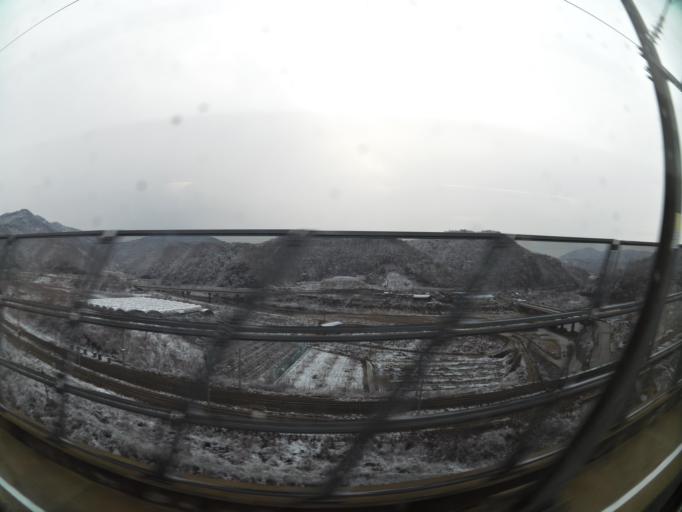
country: KR
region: Chungcheongbuk-do
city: Yong-dong
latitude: 36.2042
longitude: 127.7420
